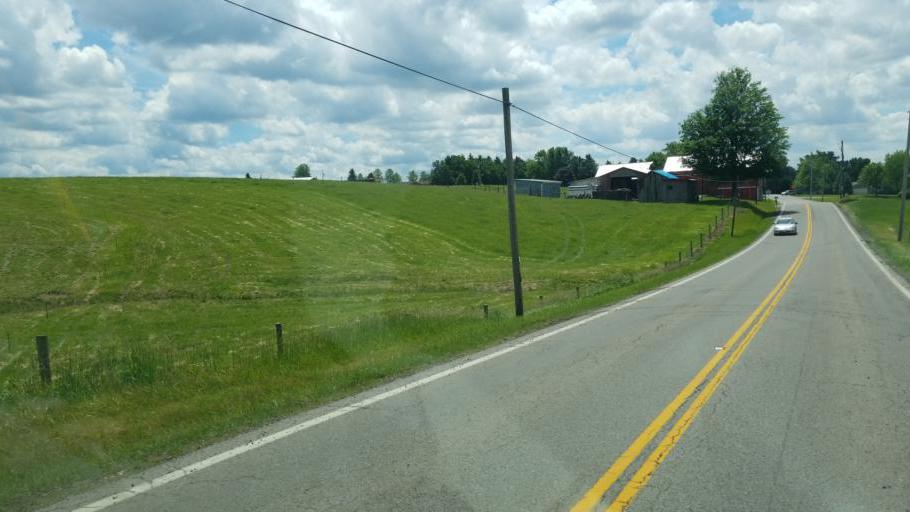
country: US
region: Ohio
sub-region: Richland County
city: Lexington
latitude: 40.6322
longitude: -82.5922
